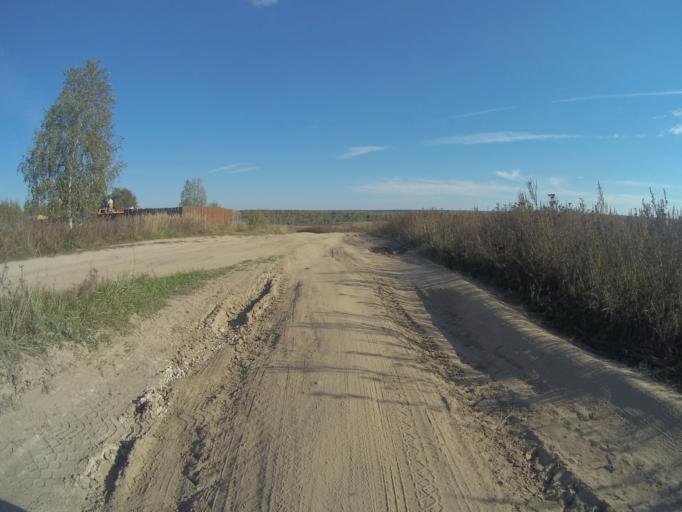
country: RU
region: Vladimir
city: Golovino
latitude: 55.9797
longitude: 40.4509
